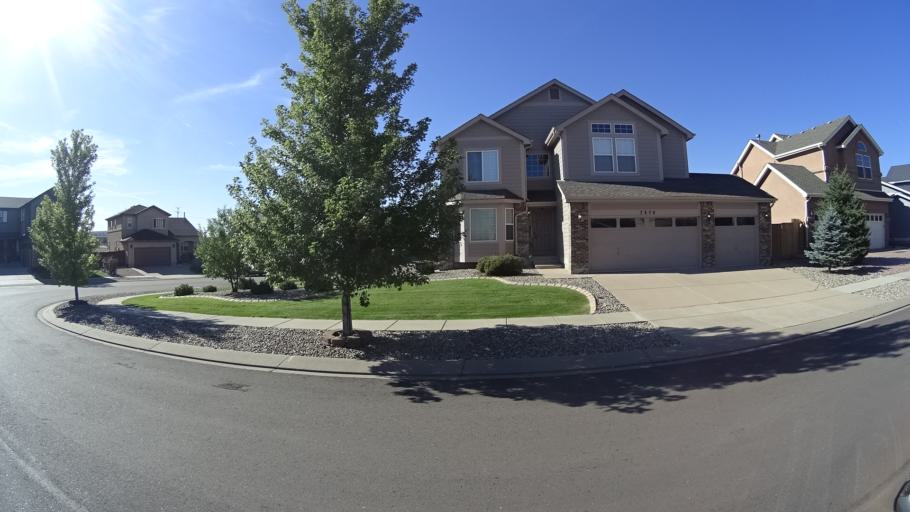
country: US
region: Colorado
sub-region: El Paso County
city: Black Forest
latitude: 38.9428
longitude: -104.7343
